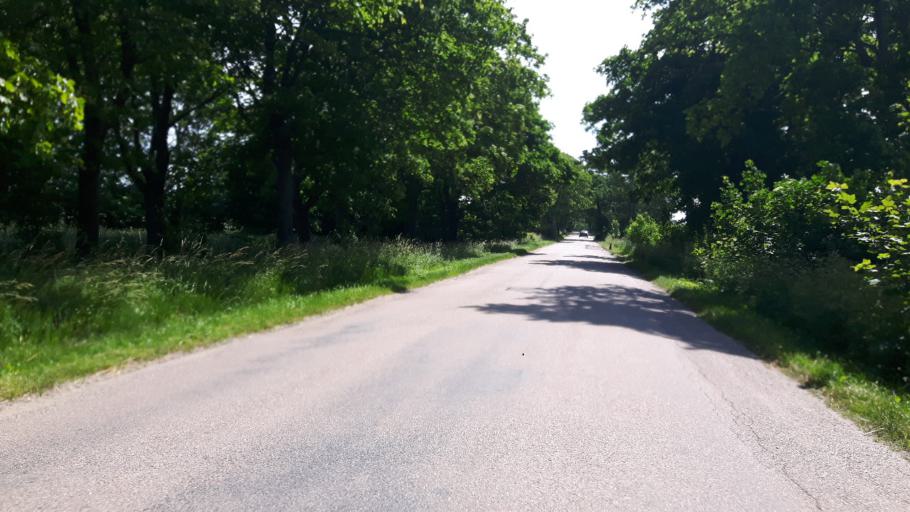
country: PL
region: Pomeranian Voivodeship
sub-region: Powiat wejherowski
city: Choczewo
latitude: 54.7444
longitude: 17.8095
